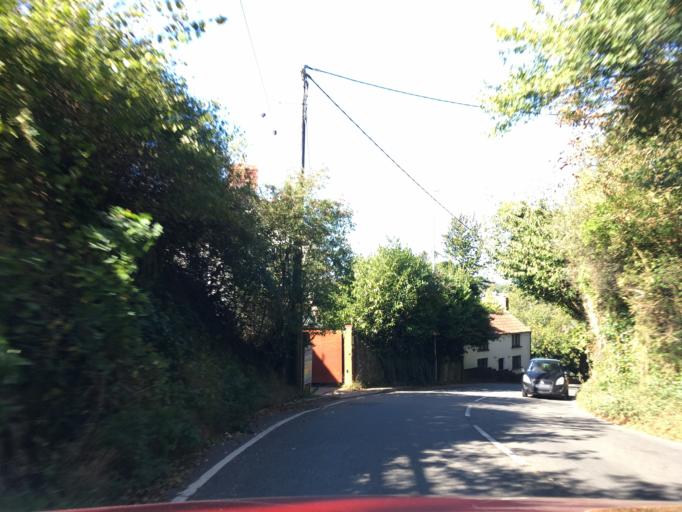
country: GB
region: Wales
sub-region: Newport
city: Caerleon
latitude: 51.6033
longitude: -2.9489
